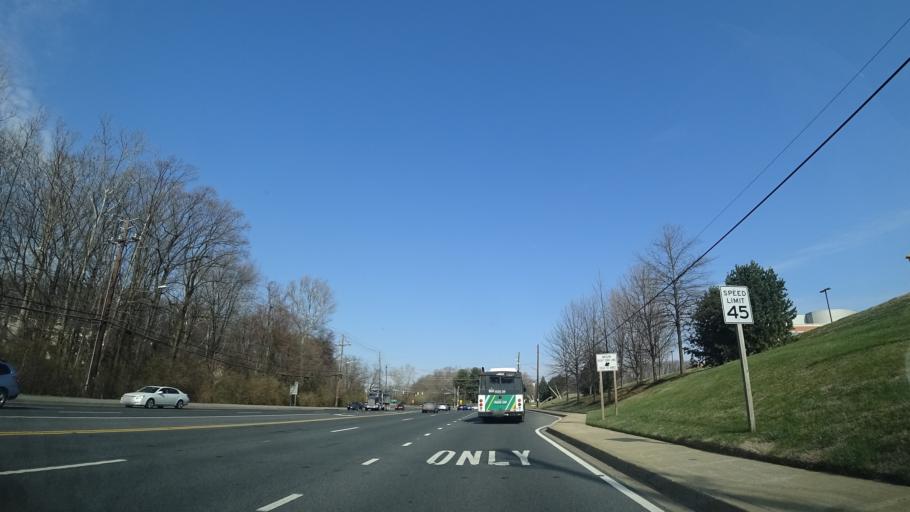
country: US
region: Maryland
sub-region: Montgomery County
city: Rockville
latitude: 39.0895
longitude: -77.1779
